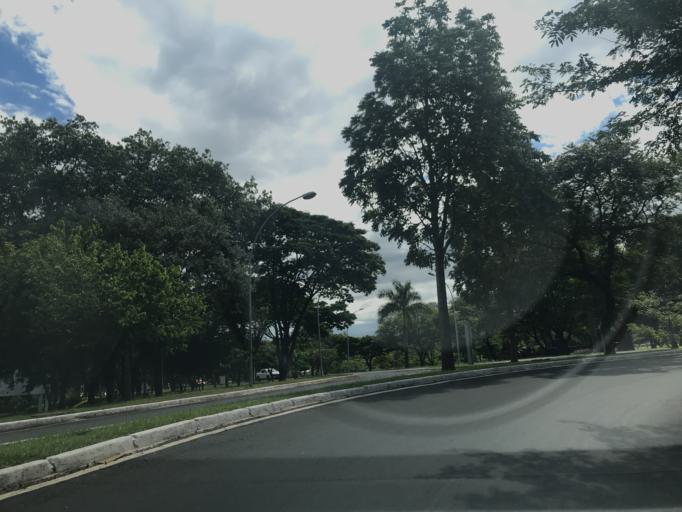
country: BR
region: Federal District
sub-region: Brasilia
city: Brasilia
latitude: -15.8222
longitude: -47.9060
